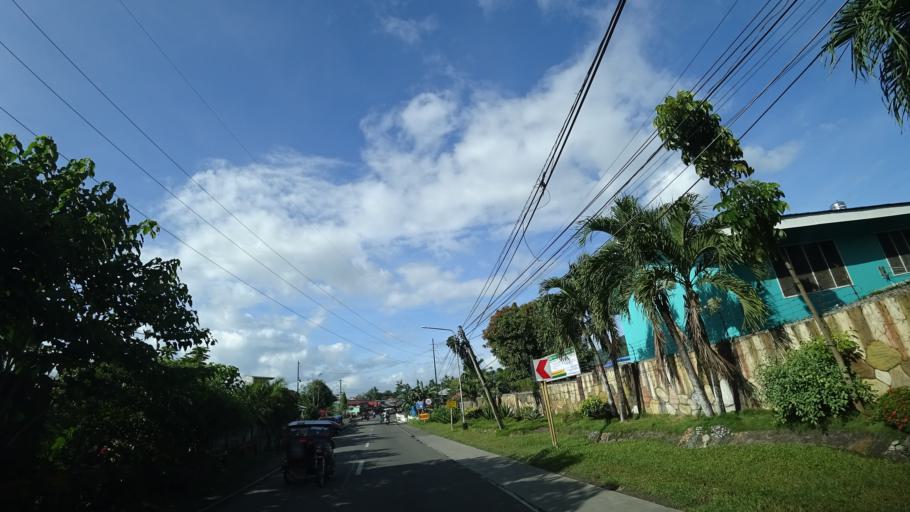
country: PH
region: Eastern Visayas
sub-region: Province of Leyte
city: Panalanoy
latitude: 11.2296
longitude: 124.9984
